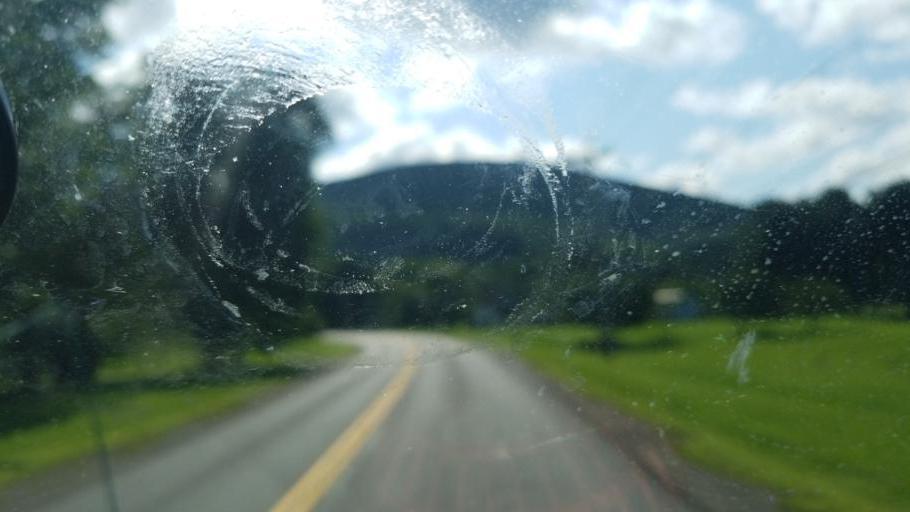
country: US
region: New York
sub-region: Steuben County
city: Canisteo
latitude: 42.2599
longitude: -77.6136
